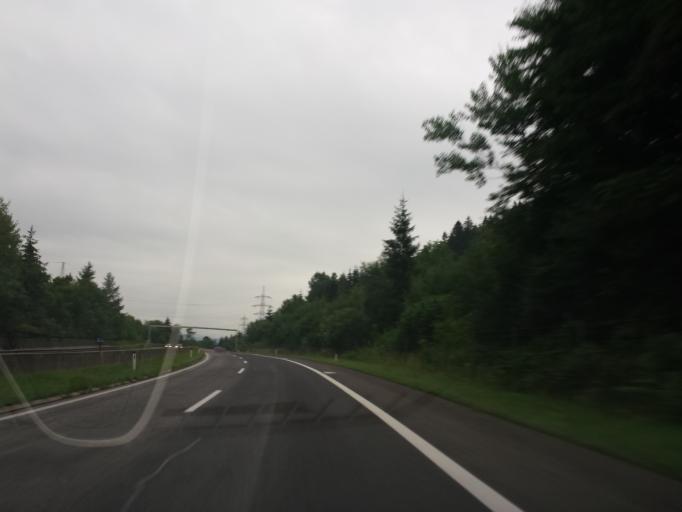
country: AT
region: Styria
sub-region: Politischer Bezirk Bruck-Muerzzuschlag
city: Mitterdorf im Muerztal
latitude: 47.5177
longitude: 15.4879
